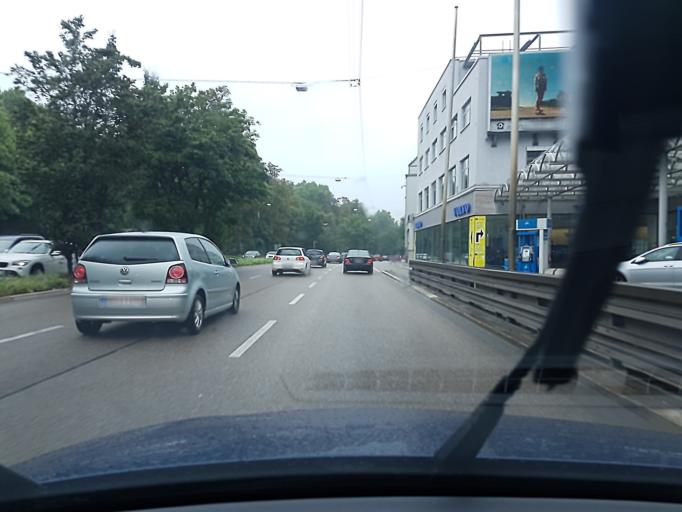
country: DE
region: Baden-Wuerttemberg
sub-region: Regierungsbezirk Stuttgart
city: Stuttgart
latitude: 48.7893
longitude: 9.1924
